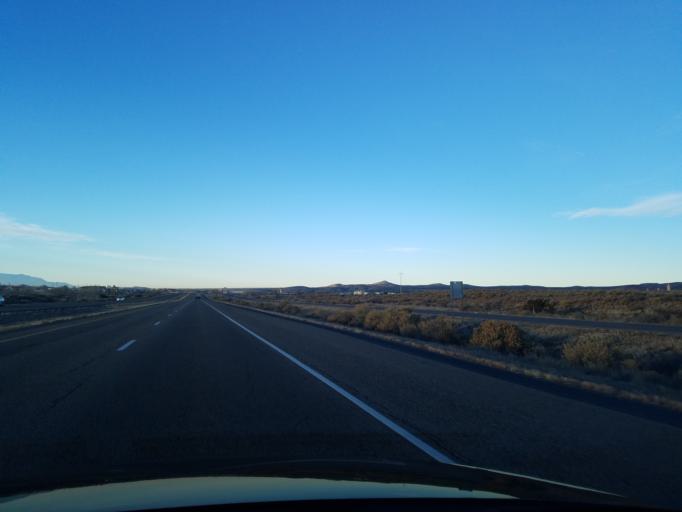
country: US
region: New Mexico
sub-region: Santa Fe County
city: Agua Fria
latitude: 35.6428
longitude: -106.0628
